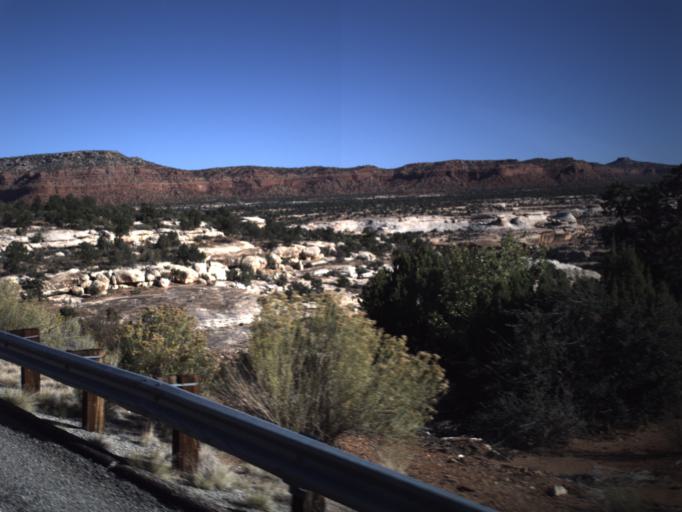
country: US
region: Utah
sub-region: San Juan County
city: Blanding
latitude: 37.6417
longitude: -110.1105
